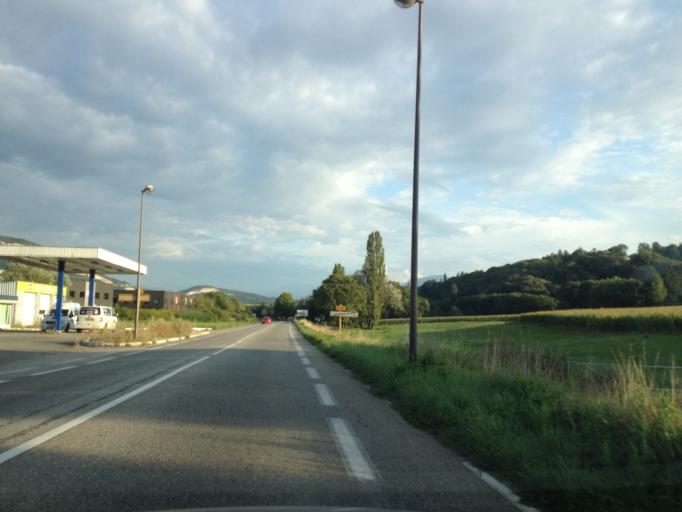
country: FR
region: Rhone-Alpes
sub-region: Departement de la Savoie
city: Viviers-du-Lac
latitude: 45.6468
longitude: 5.9097
